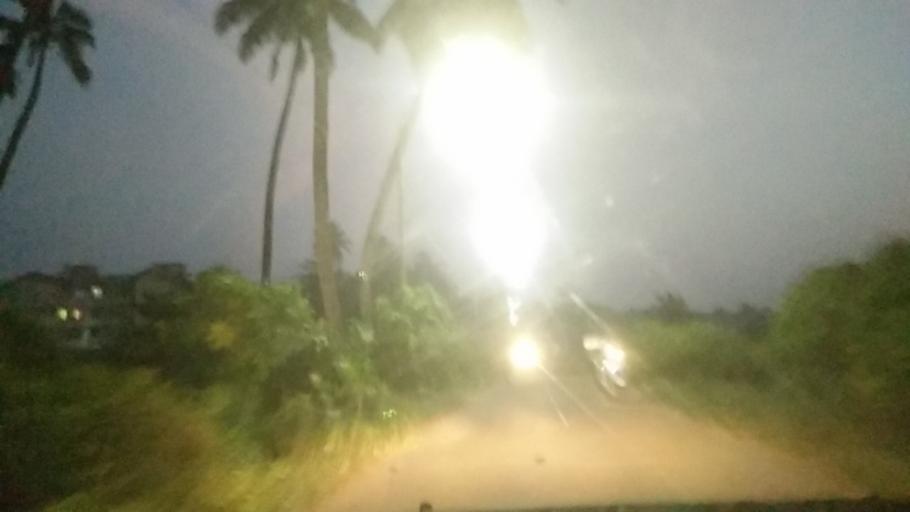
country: IN
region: Goa
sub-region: South Goa
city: Madgaon
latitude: 15.2662
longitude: 73.9647
